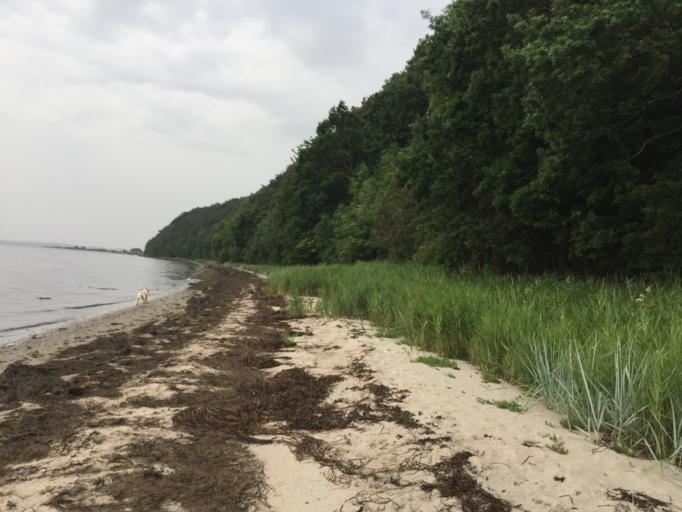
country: DK
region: South Denmark
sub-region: Assens Kommune
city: Harby
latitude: 55.1441
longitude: 10.0312
